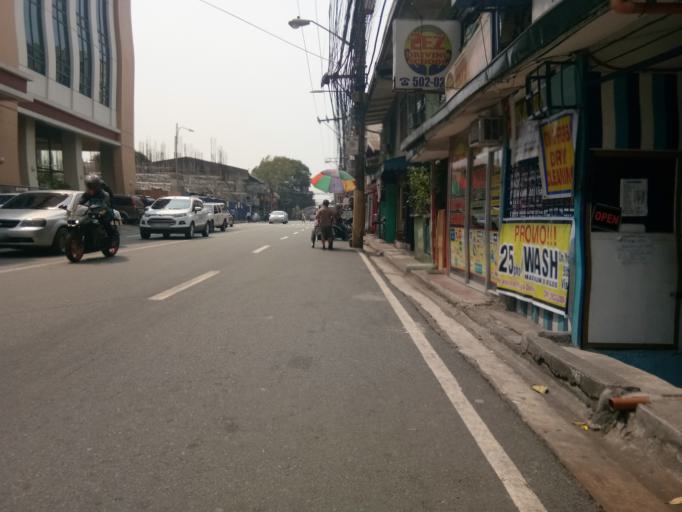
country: PH
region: Metro Manila
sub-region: San Juan
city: San Juan
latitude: 14.6097
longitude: 121.0500
